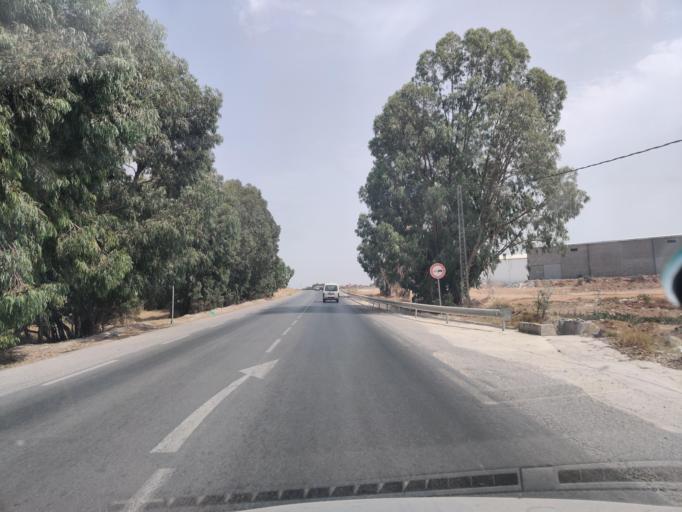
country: TN
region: Nabul
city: Bu `Urqub
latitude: 36.4641
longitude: 10.5714
